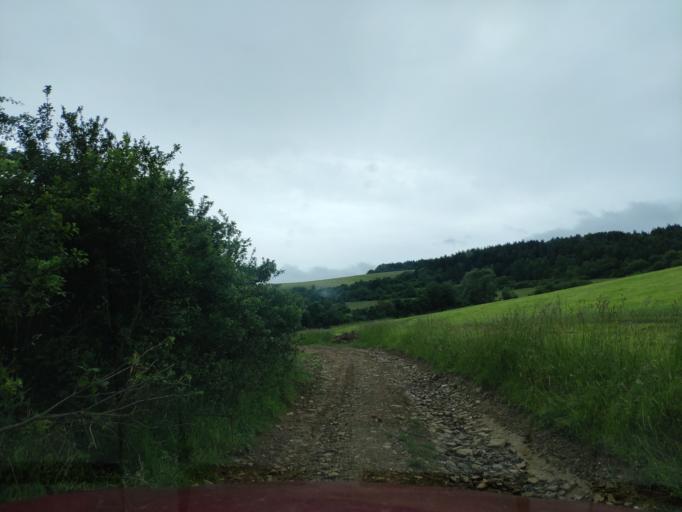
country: SK
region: Presovsky
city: Sabinov
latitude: 49.0502
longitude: 21.0094
